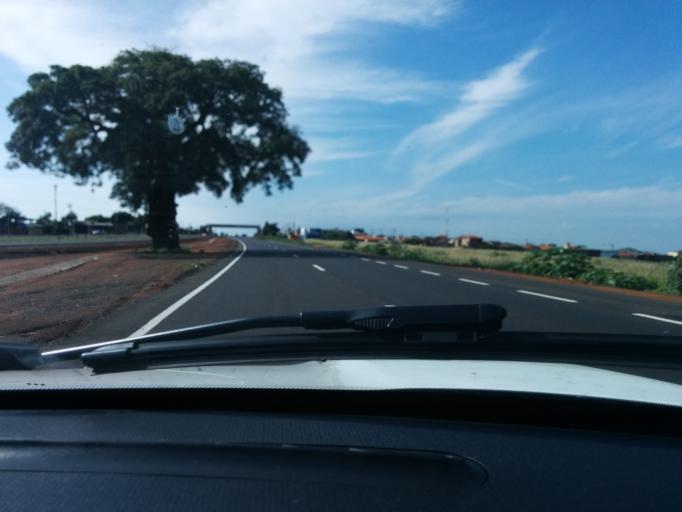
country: BR
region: Sao Paulo
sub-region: Franca
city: Franca
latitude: -20.4668
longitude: -47.4143
